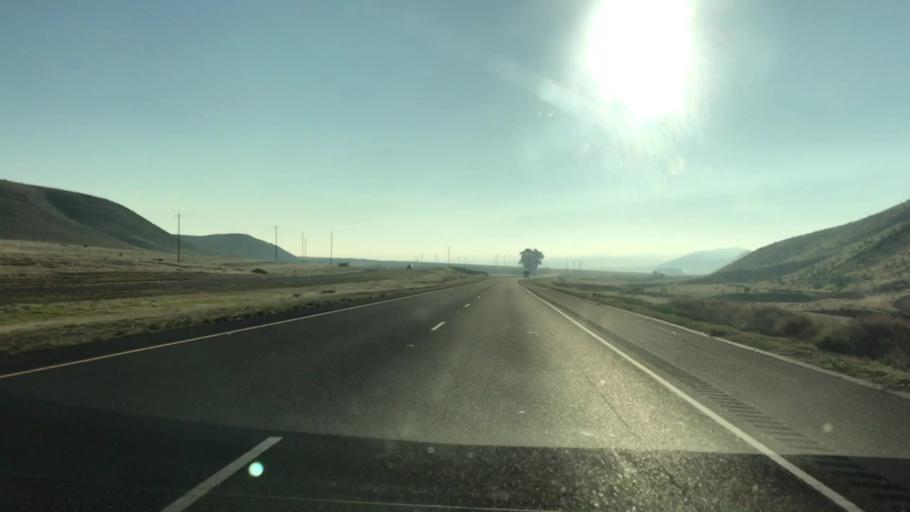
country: US
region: California
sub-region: San Luis Obispo County
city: Shandon
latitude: 35.7167
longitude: -120.1733
